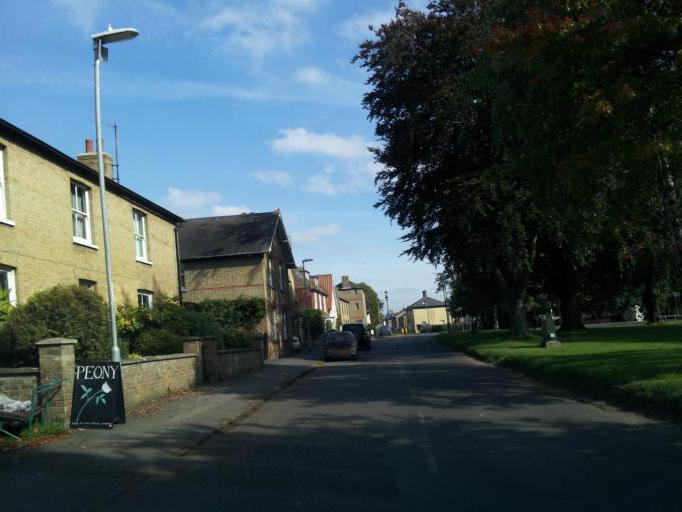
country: GB
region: England
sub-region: Cambridgeshire
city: Cottenham
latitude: 52.2833
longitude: 0.1217
